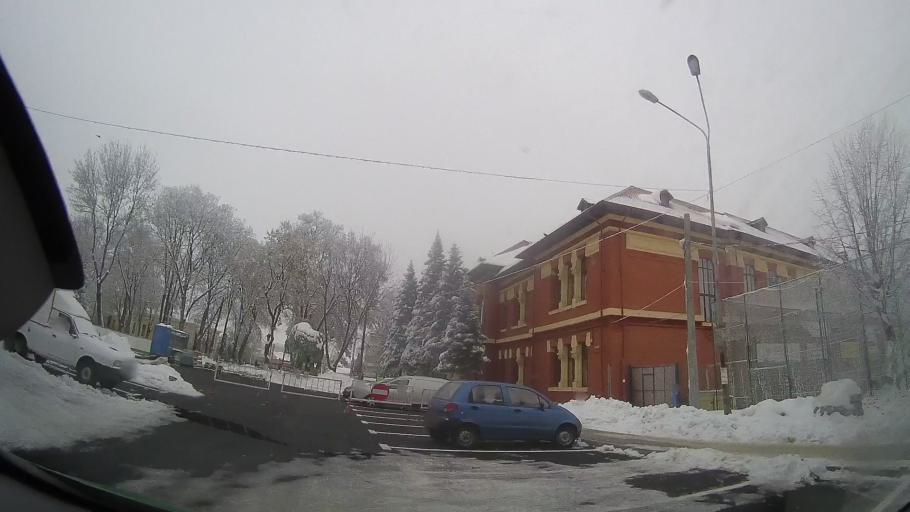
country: RO
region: Neamt
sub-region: Municipiul Roman
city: Roman
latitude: 46.9252
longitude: 26.9305
